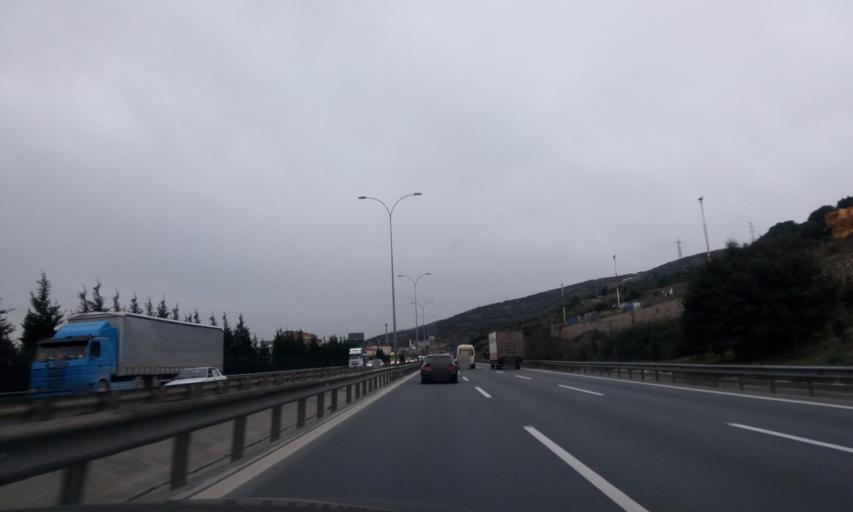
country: TR
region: Kocaeli
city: Korfez
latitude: 40.7757
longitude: 29.7558
